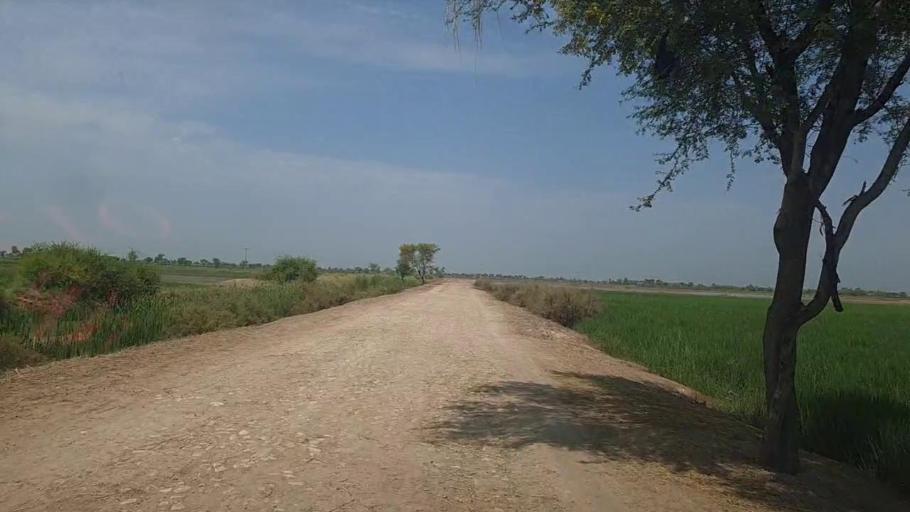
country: PK
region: Sindh
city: Thul
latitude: 28.2978
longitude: 68.6793
